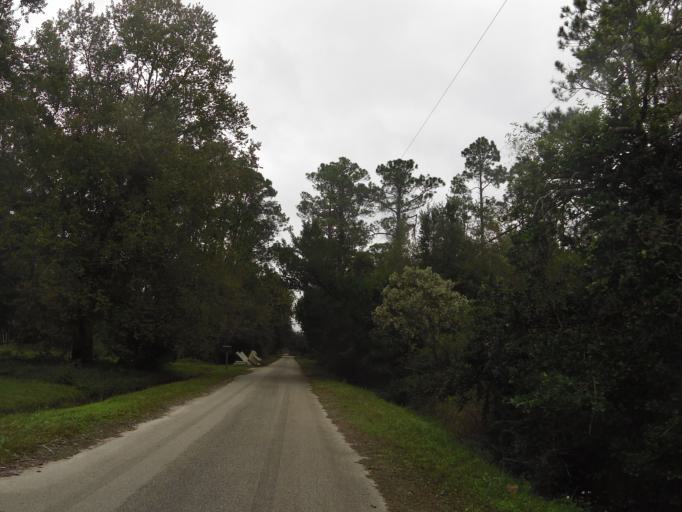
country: US
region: Florida
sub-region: Duval County
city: Baldwin
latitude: 30.2584
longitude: -81.8739
